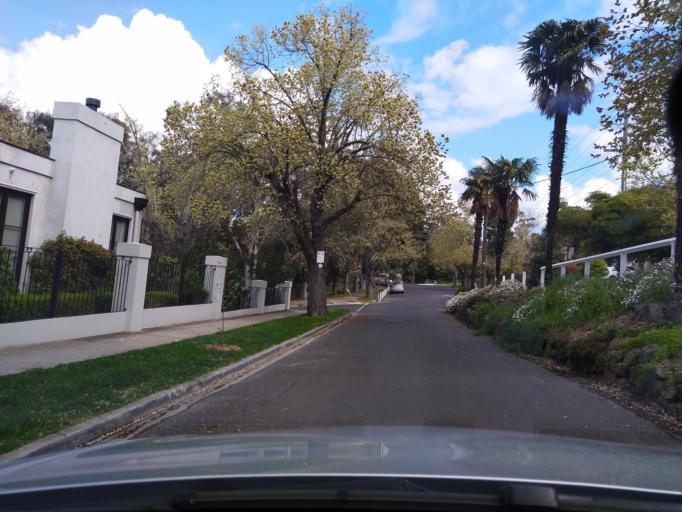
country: AU
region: Victoria
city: Rosanna
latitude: -37.7611
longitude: 145.0611
